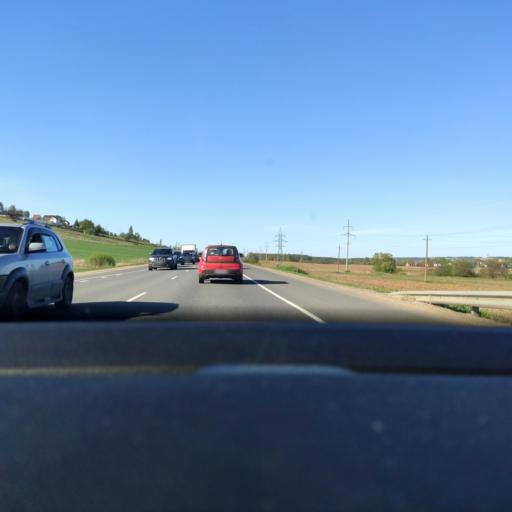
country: RU
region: Moskovskaya
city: Dmitrov
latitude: 56.3398
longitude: 37.4829
